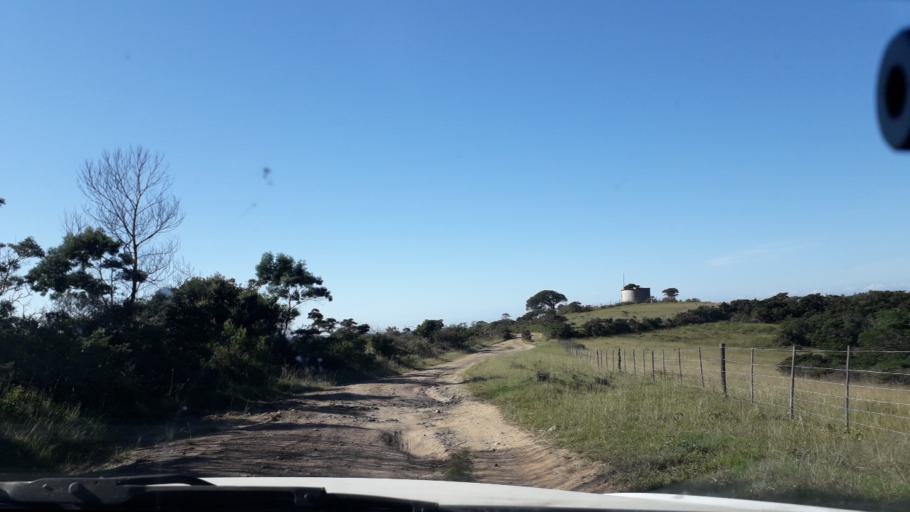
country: ZA
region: Eastern Cape
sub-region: Buffalo City Metropolitan Municipality
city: East London
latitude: -32.8410
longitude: 27.9797
